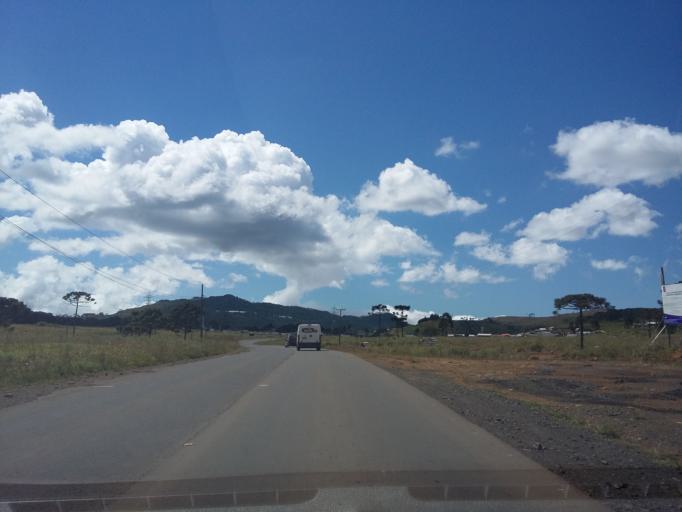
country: BR
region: Santa Catarina
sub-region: Lauro Muller
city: Lauro Muller
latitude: -28.3396
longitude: -49.6408
